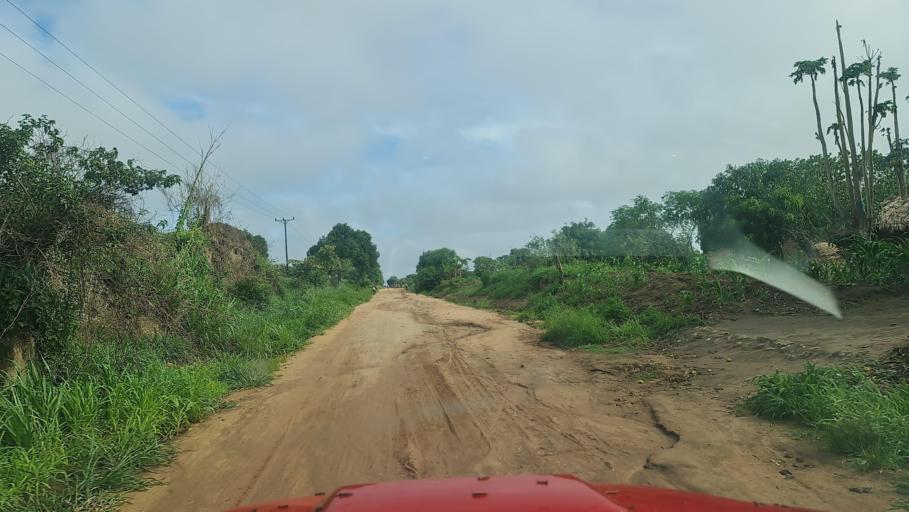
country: MW
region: Southern Region
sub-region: Nsanje District
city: Nsanje
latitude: -17.3069
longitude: 35.5930
